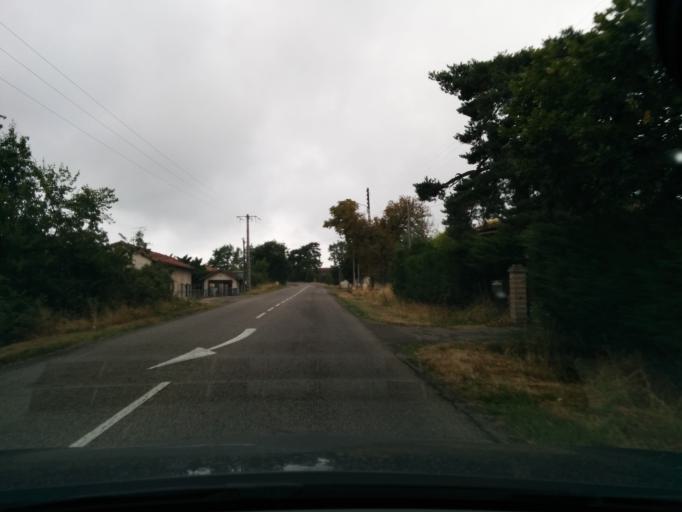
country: FR
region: Midi-Pyrenees
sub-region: Departement du Tarn-et-Garonne
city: Moissac
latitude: 44.1163
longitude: 1.0741
